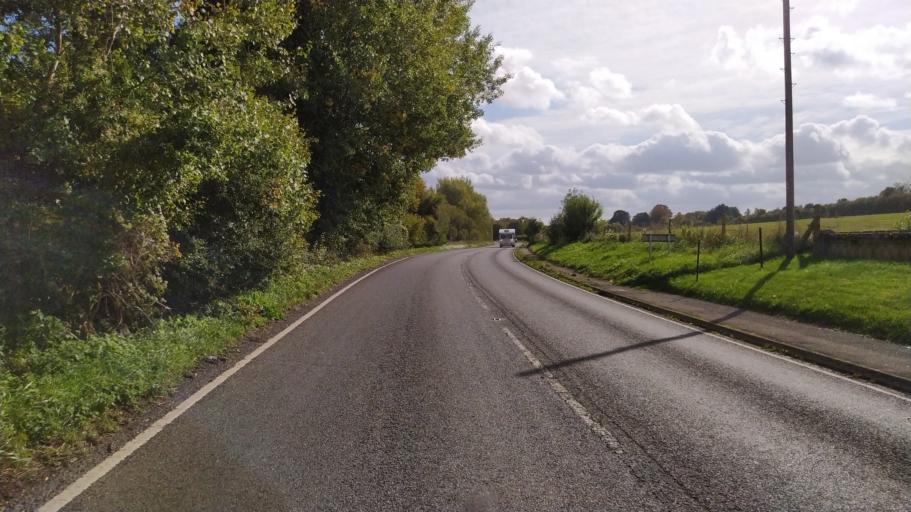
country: GB
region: England
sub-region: Hampshire
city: Kings Worthy
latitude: 51.1660
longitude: -1.3380
